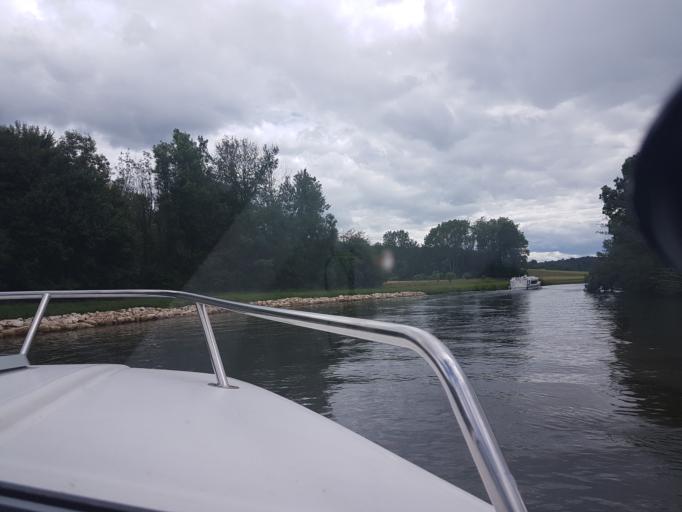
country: FR
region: Bourgogne
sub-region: Departement de l'Yonne
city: Vermenton
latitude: 47.5783
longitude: 3.6500
